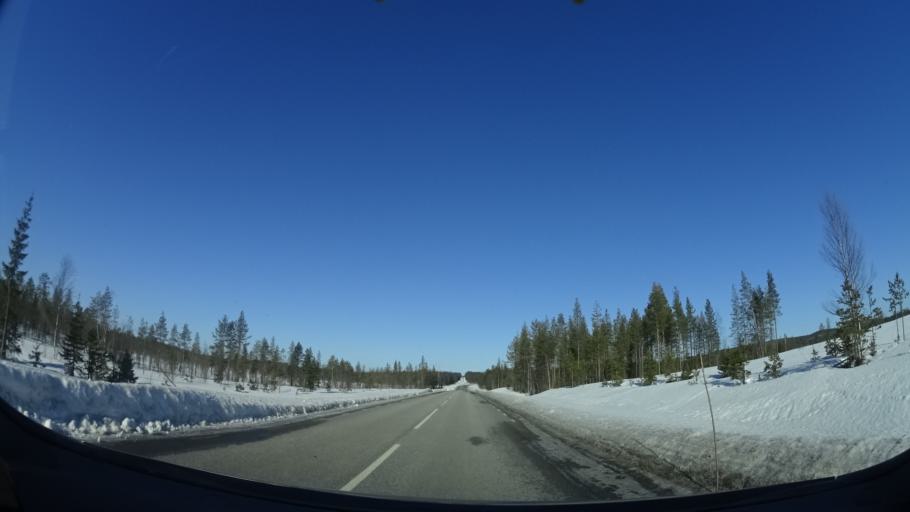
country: SE
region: Vaesterbotten
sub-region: Skelleftea Kommun
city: Langsele
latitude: 65.1043
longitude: 20.0823
